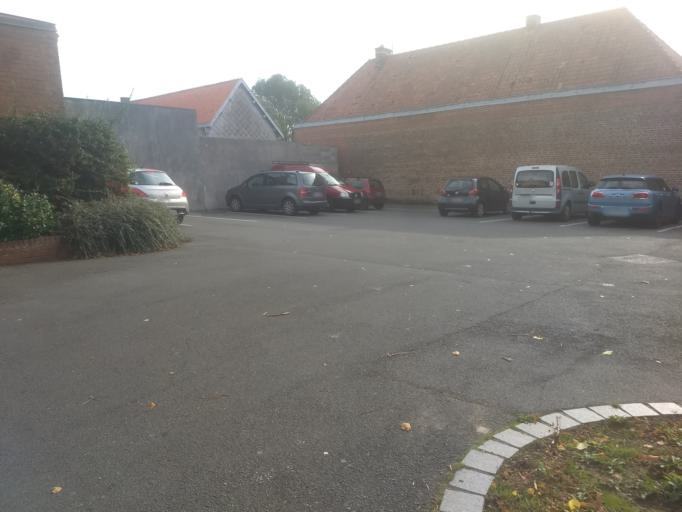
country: FR
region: Nord-Pas-de-Calais
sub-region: Departement du Pas-de-Calais
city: Dainville
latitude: 50.2809
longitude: 2.7228
